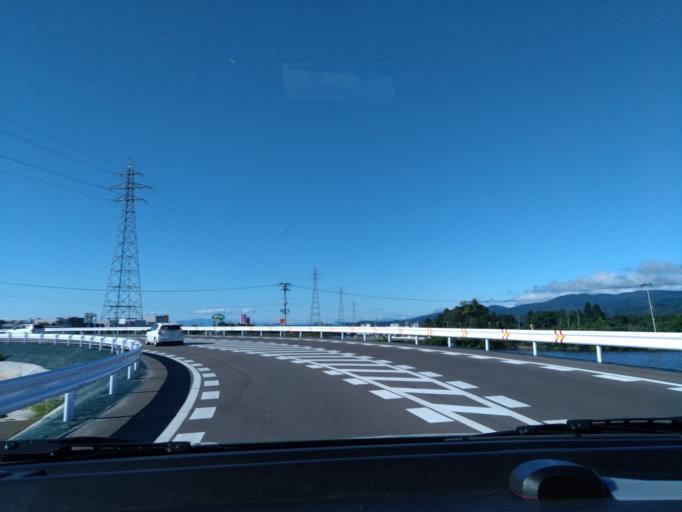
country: JP
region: Akita
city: Yokotemachi
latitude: 39.2904
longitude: 140.5539
